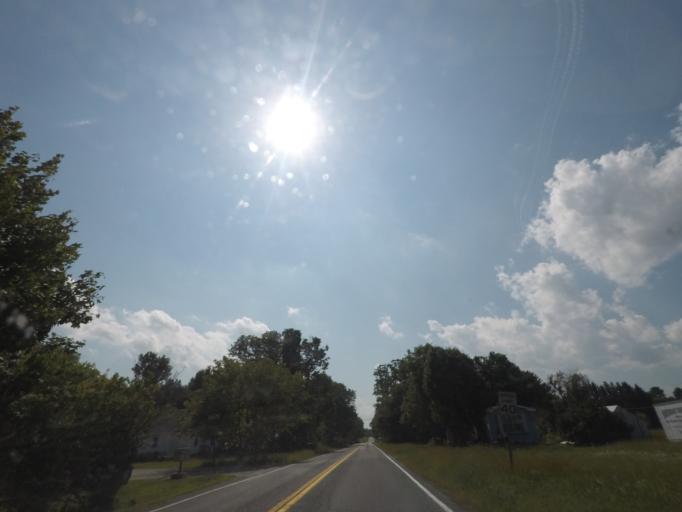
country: US
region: New York
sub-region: Rensselaer County
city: Poestenkill
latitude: 42.8124
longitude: -73.5079
